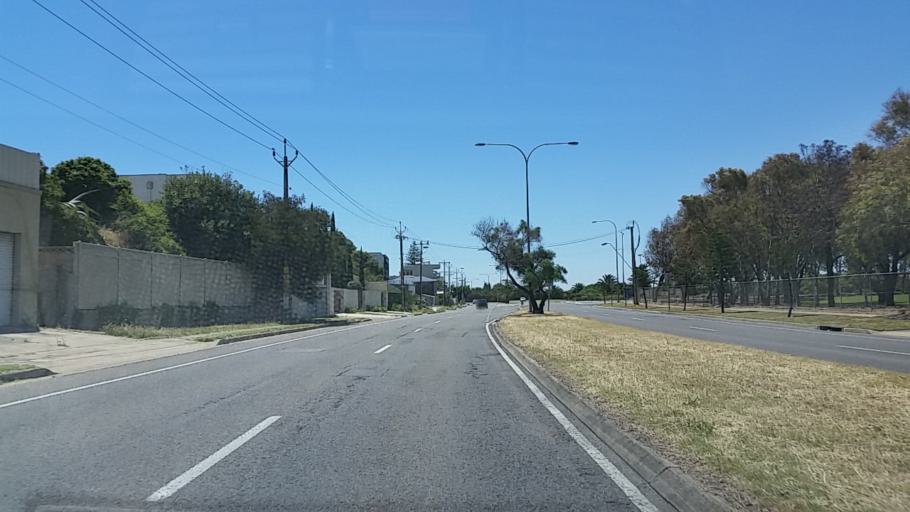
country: AU
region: South Australia
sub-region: Charles Sturt
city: Grange
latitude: -34.8958
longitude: 138.4890
